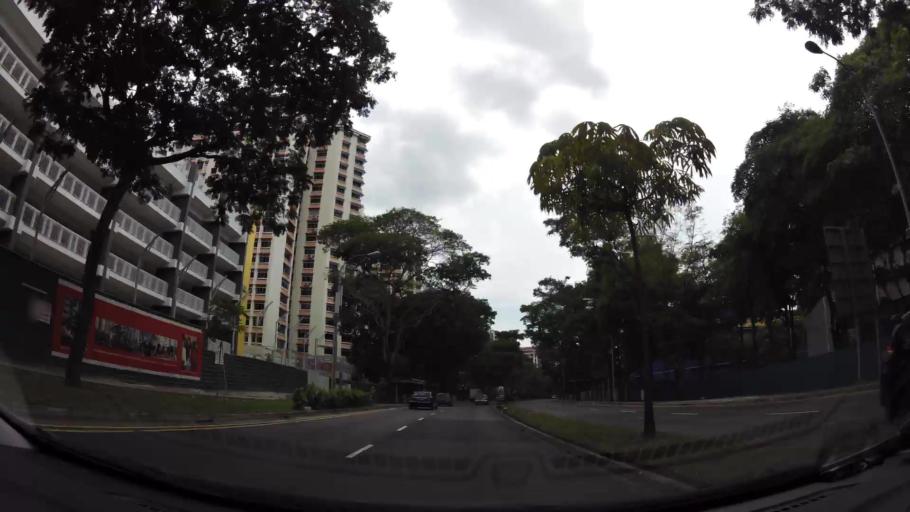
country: SG
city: Singapore
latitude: 1.3305
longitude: 103.7211
